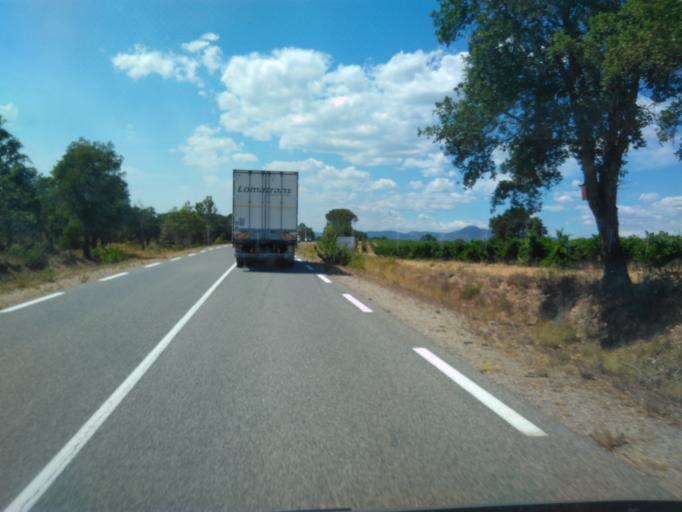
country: FR
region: Provence-Alpes-Cote d'Azur
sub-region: Departement du Var
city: La Garde-Freinet
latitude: 43.3564
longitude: 6.4081
